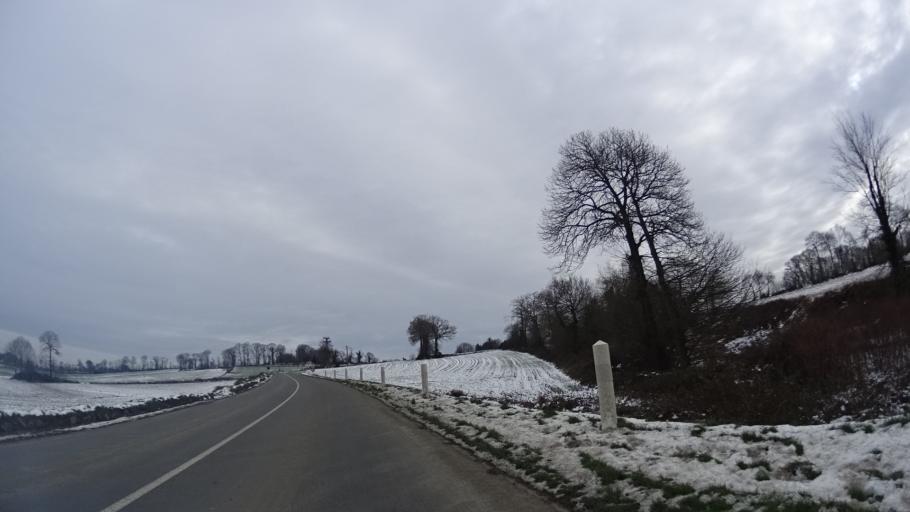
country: FR
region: Brittany
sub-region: Departement d'Ille-et-Vilaine
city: Irodouer
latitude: 48.3055
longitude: -1.9455
